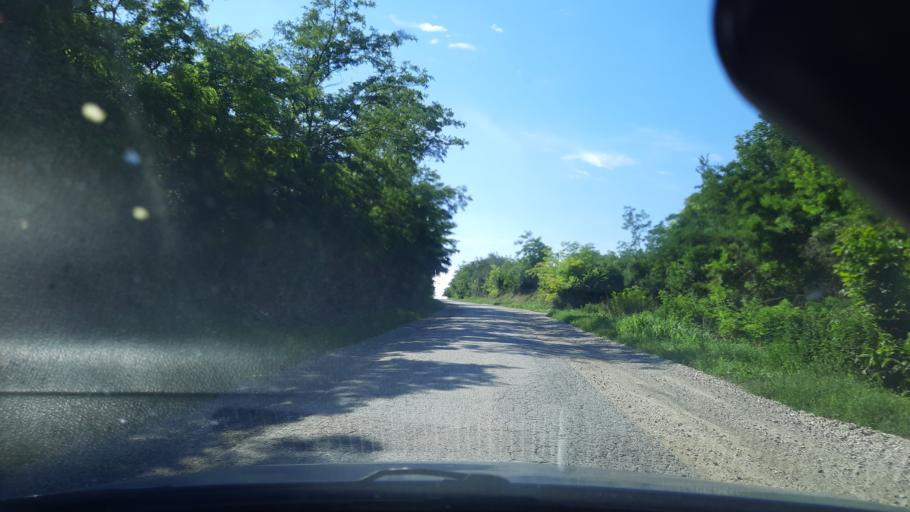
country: RS
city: Cortanovci
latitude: 45.1059
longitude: 19.9844
